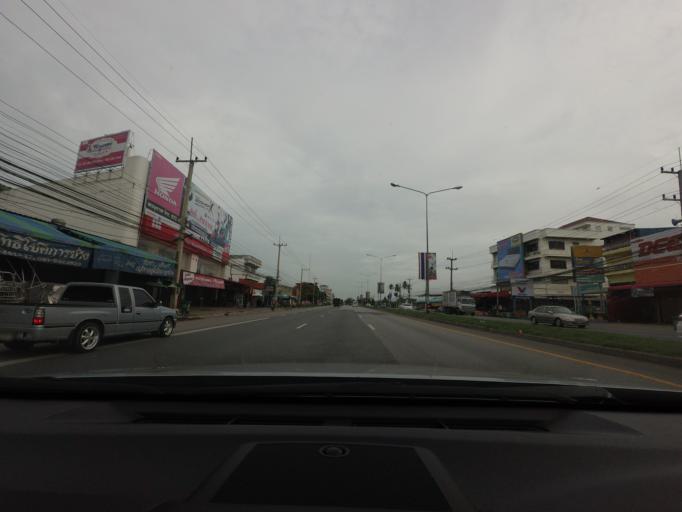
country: TH
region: Phetchaburi
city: Tha Yang
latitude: 12.9653
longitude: 99.9001
